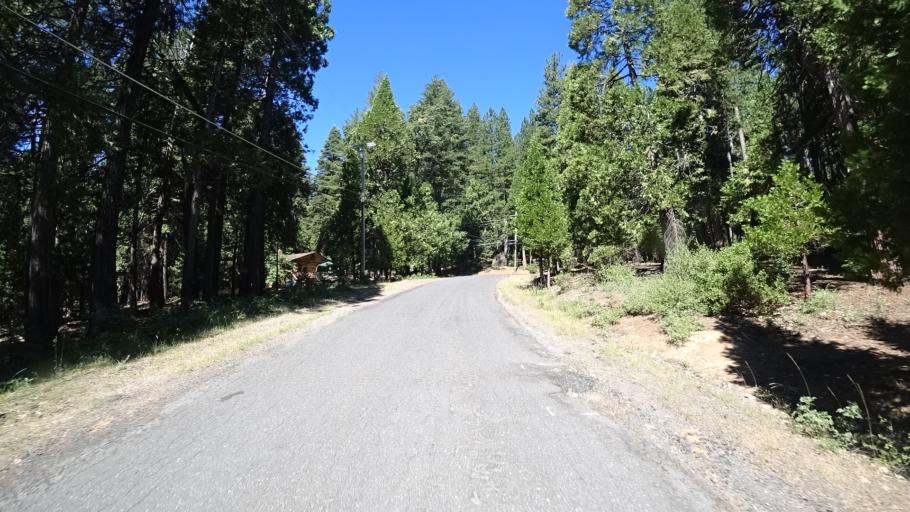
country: US
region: California
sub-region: Calaveras County
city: Arnold
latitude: 38.2871
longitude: -120.2799
